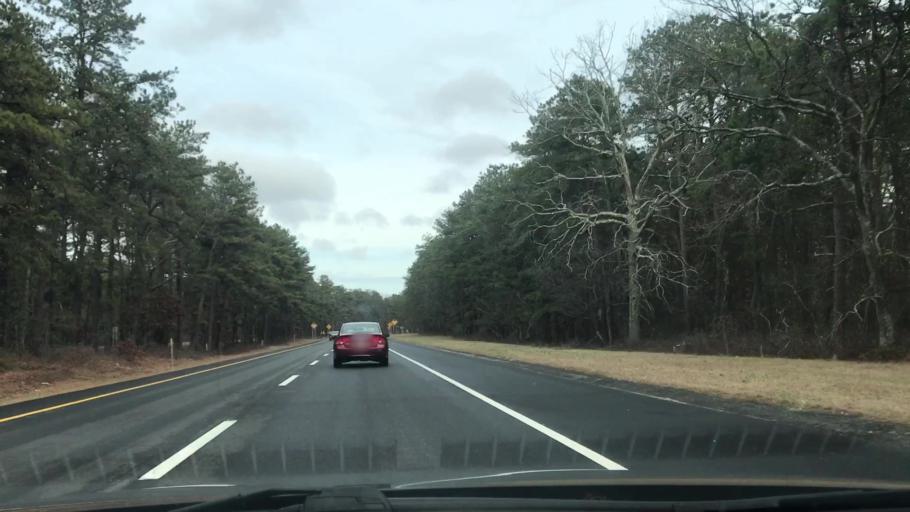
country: US
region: New York
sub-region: Suffolk County
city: Riverhead
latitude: 40.9128
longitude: -72.6804
